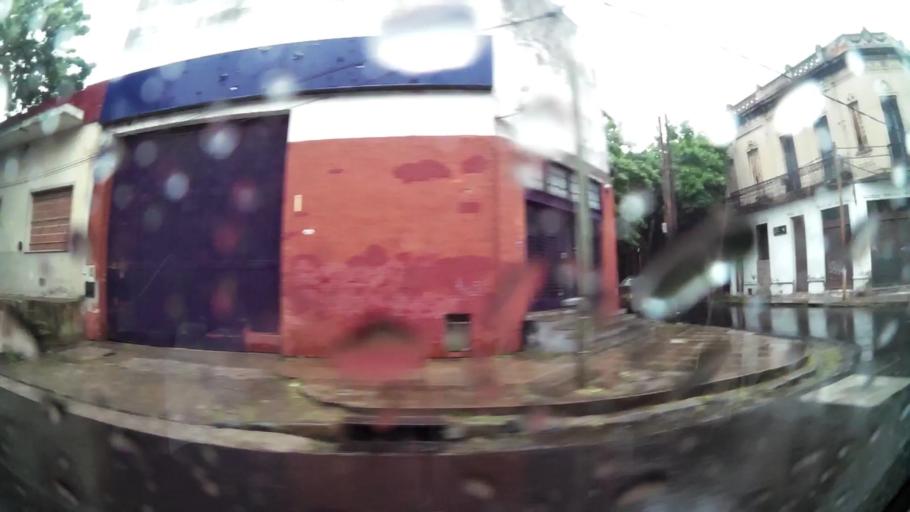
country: AR
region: Buenos Aires
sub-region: Partido de Avellaneda
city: Avellaneda
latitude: -34.6435
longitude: -58.3656
